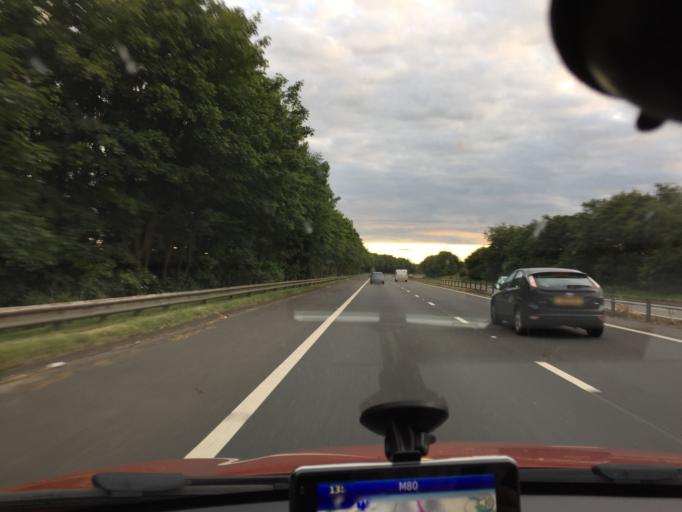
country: GB
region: Scotland
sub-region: Falkirk
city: Bonnybridge
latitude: 56.0039
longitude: -3.9012
